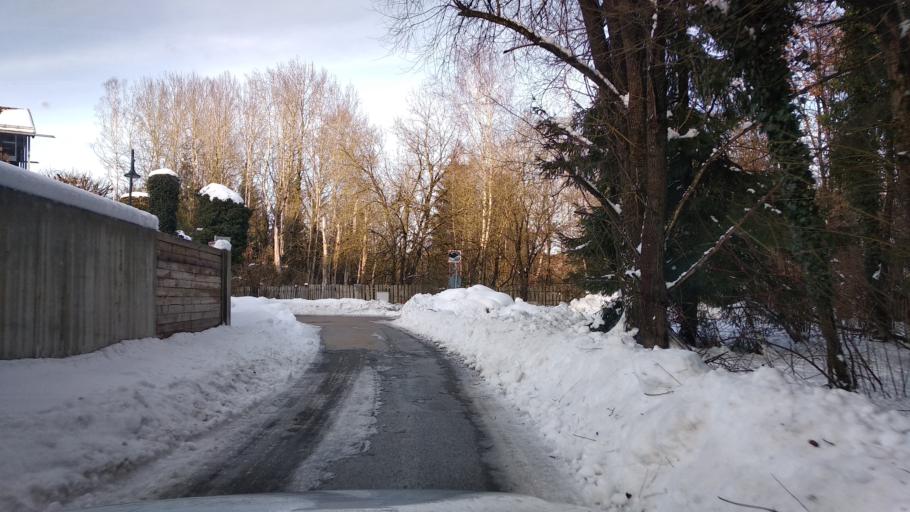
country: DE
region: Bavaria
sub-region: Upper Bavaria
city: Kirchseeon
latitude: 48.0711
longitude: 11.8808
